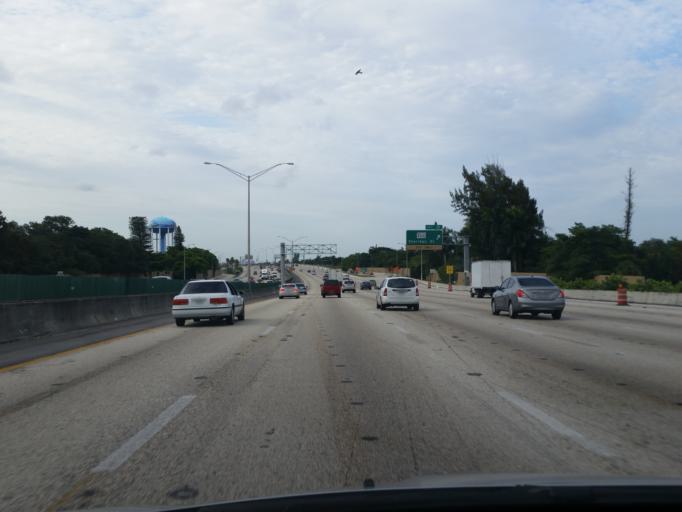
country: US
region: Florida
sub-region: Broward County
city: Hollywood
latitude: 26.0269
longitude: -80.1663
